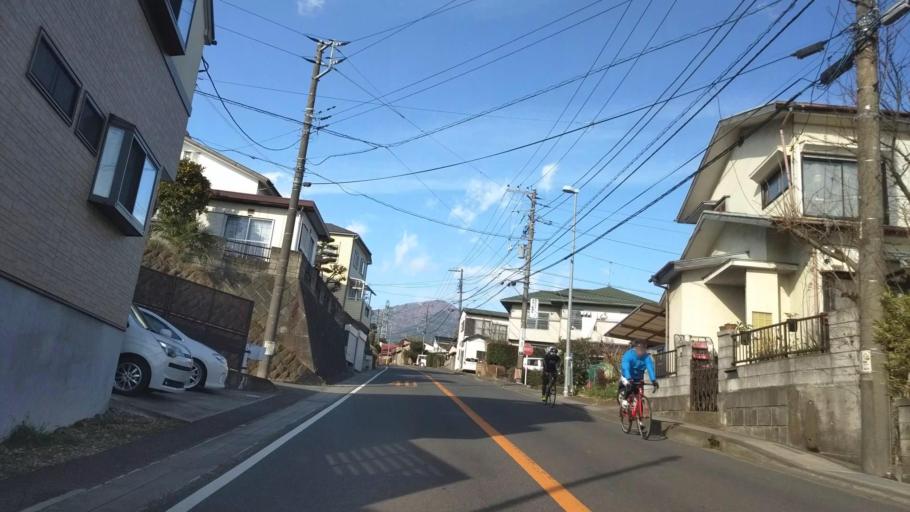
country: JP
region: Kanagawa
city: Hadano
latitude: 35.3838
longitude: 139.2378
